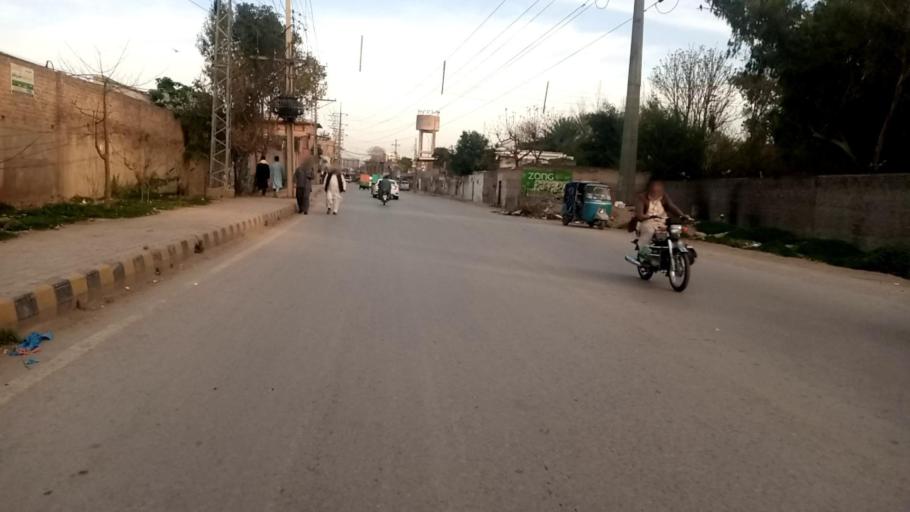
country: PK
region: Khyber Pakhtunkhwa
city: Peshawar
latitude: 34.0199
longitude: 71.5661
